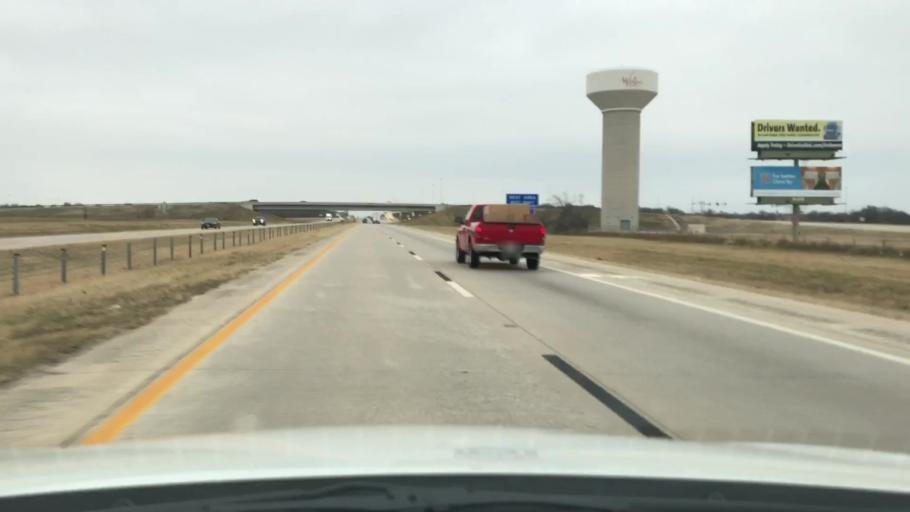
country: US
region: Texas
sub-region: Cooke County
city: Gainesville
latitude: 33.7630
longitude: -97.1348
